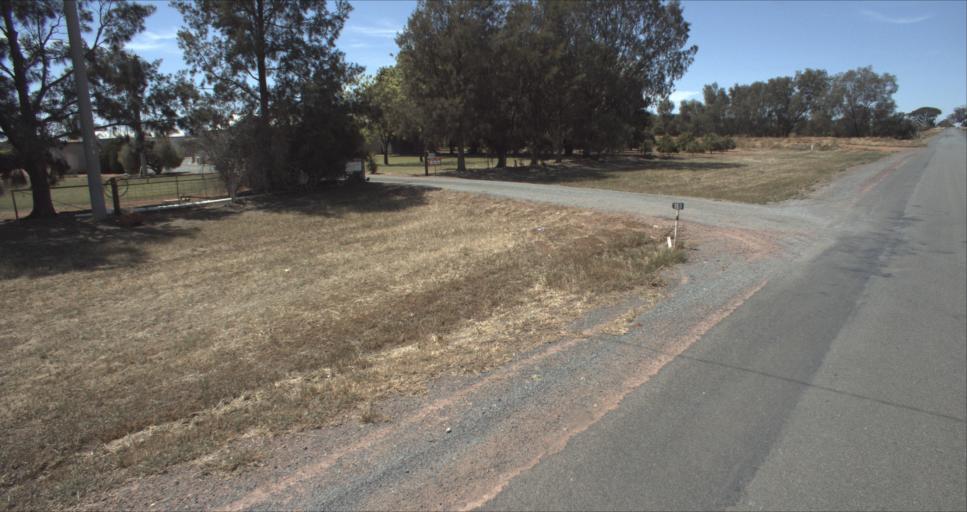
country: AU
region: New South Wales
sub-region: Leeton
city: Leeton
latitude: -34.6118
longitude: 146.4253
